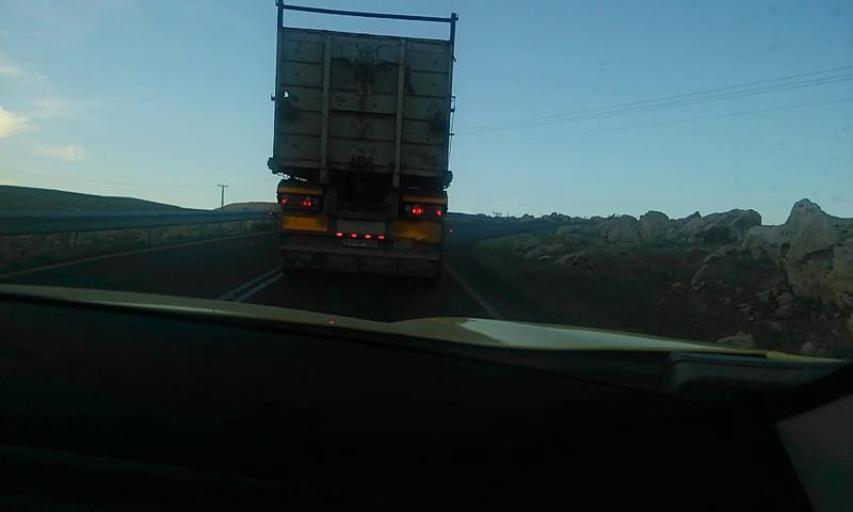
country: PS
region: West Bank
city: Rammun
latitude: 31.9166
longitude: 35.3482
